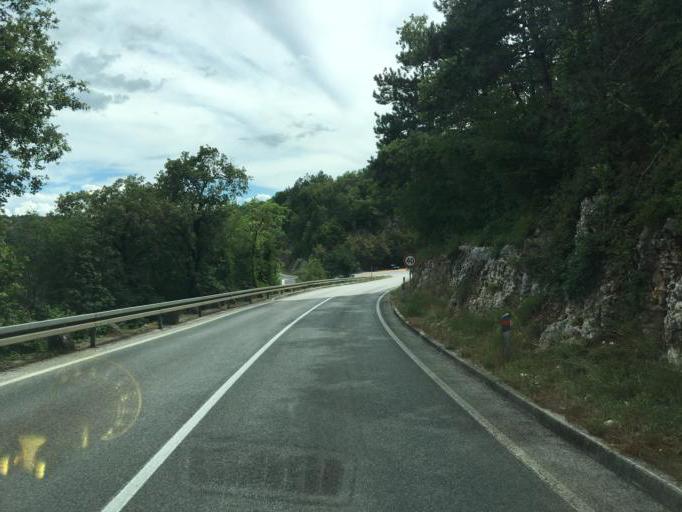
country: HR
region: Istarska
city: Pazin
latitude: 45.2507
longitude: 13.8822
